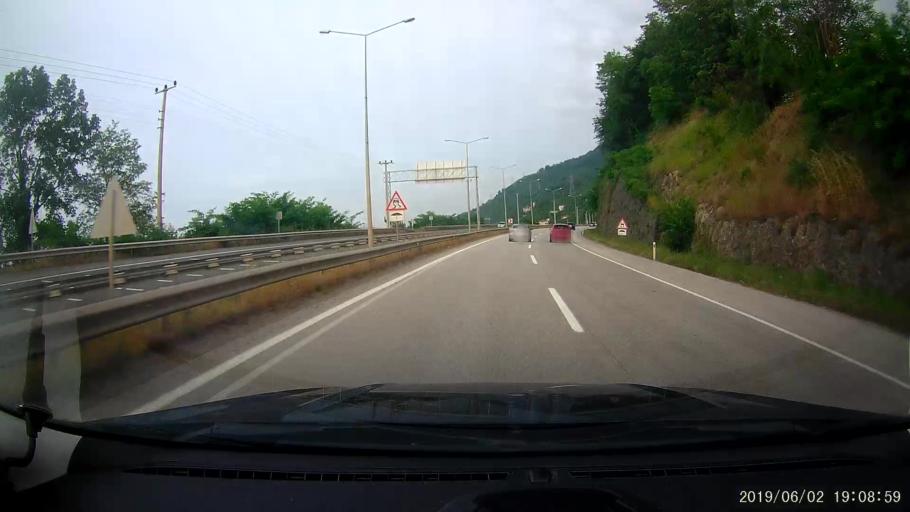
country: TR
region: Ordu
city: Gulyali
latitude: 40.9760
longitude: 38.0200
